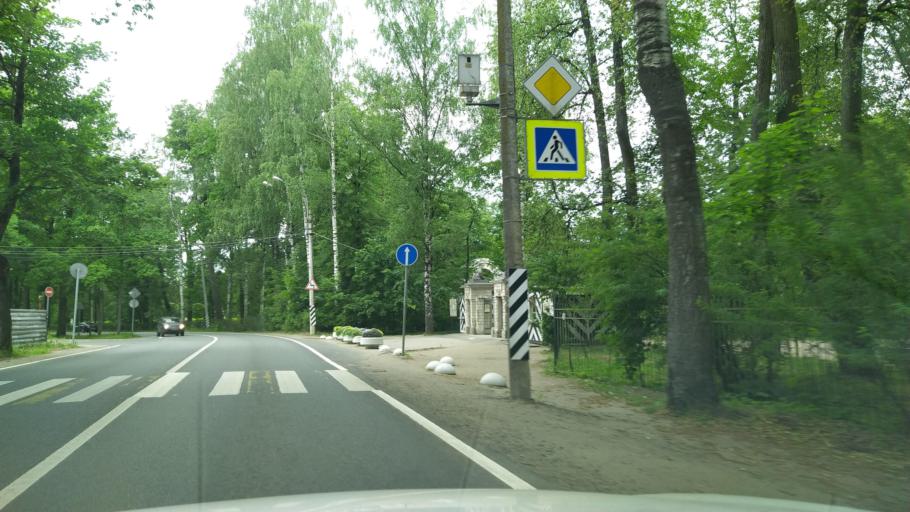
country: RU
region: St.-Petersburg
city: Tyarlevo
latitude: 59.6853
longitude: 30.4606
